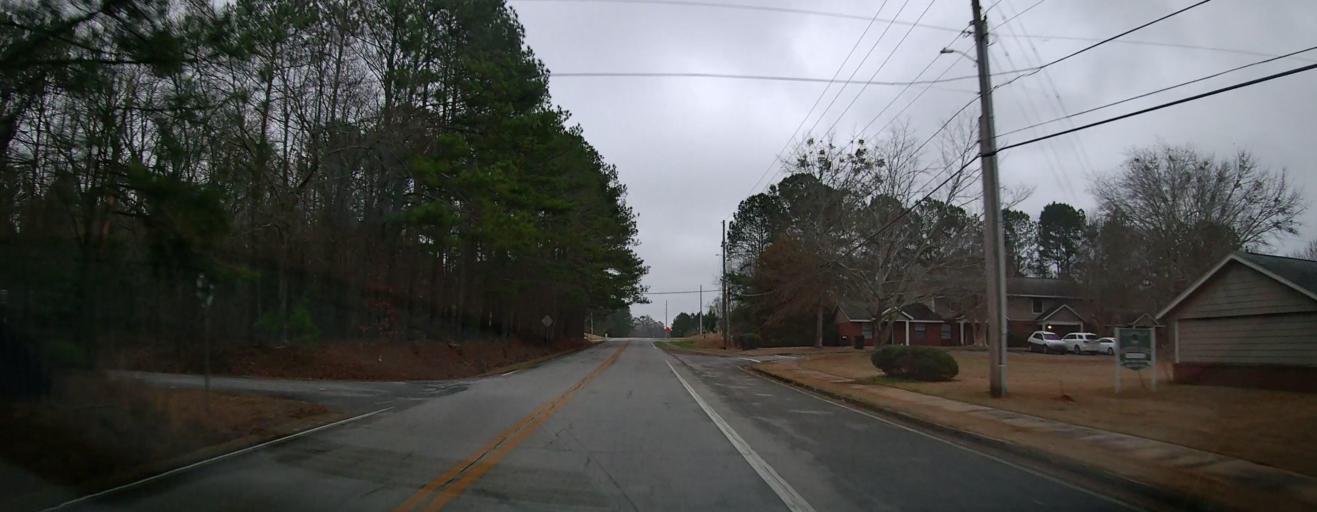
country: US
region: Georgia
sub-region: Lamar County
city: Barnesville
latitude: 33.0542
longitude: -84.1343
